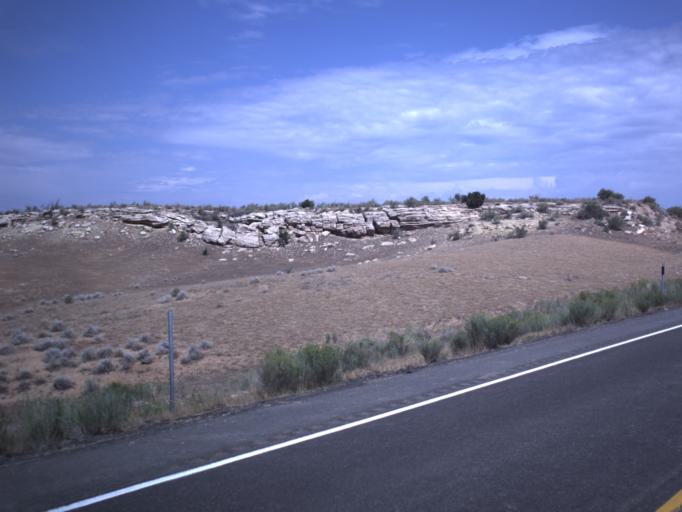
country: US
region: Utah
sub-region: Uintah County
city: Naples
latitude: 40.1912
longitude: -109.3310
